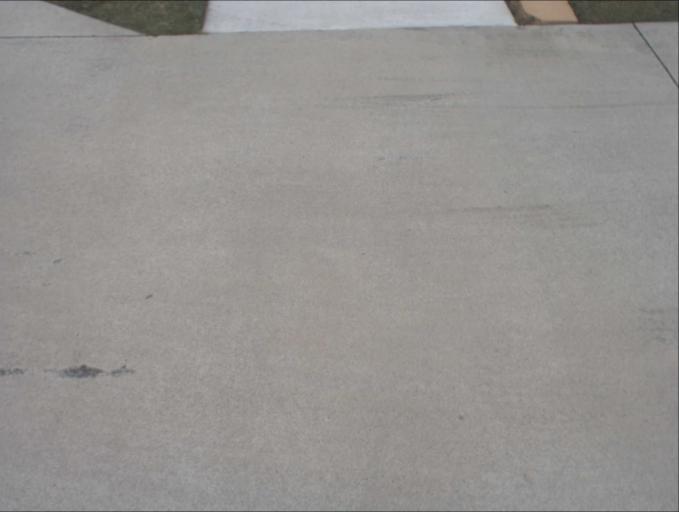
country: AU
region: Queensland
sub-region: Logan
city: Park Ridge South
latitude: -27.6966
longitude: 153.0266
